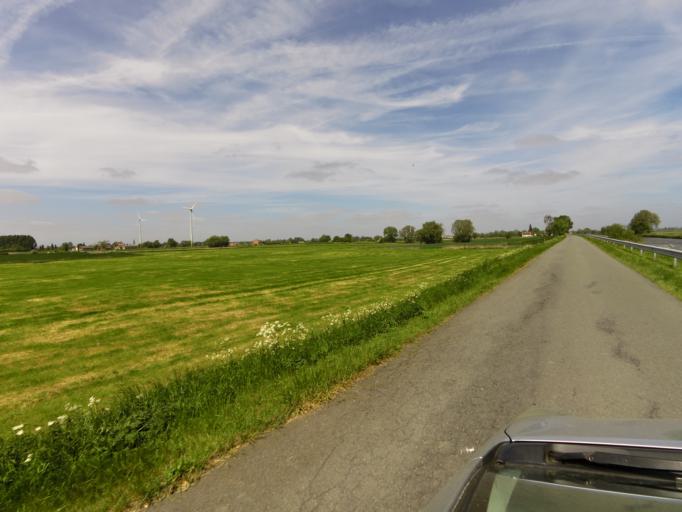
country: BE
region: Flanders
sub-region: Provincie West-Vlaanderen
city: Diksmuide
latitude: 50.9869
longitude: 2.8119
